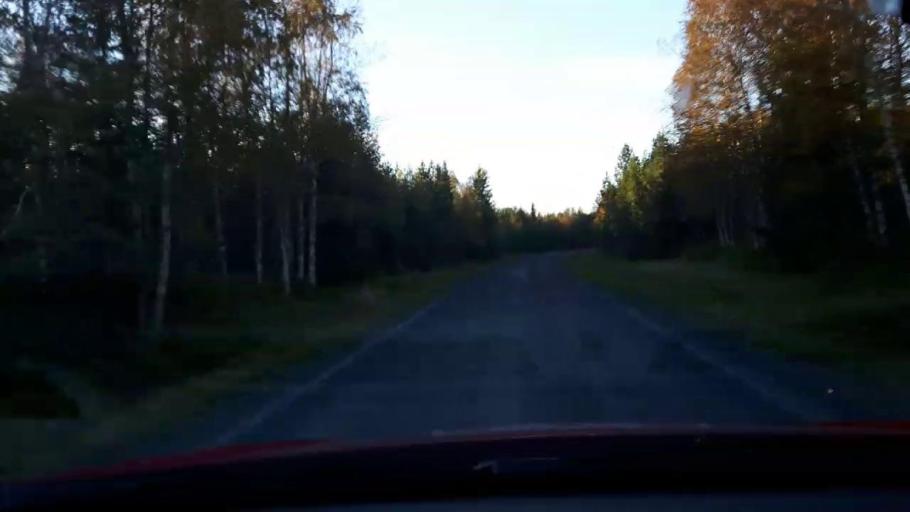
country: SE
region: Jaemtland
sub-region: Krokoms Kommun
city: Krokom
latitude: 63.4413
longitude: 14.5945
